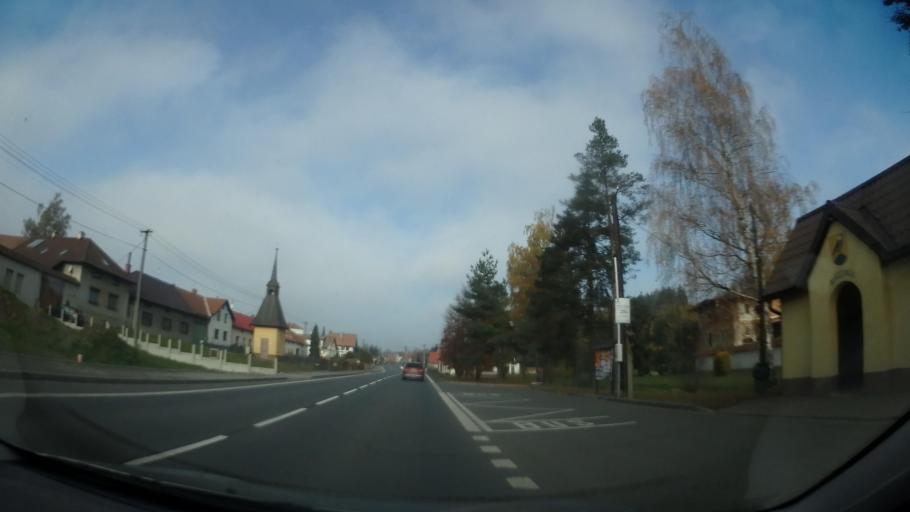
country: CZ
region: Vysocina
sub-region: Okres Zd'ar nad Sazavou
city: Zd'ar nad Sazavou
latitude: 49.5080
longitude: 15.9825
